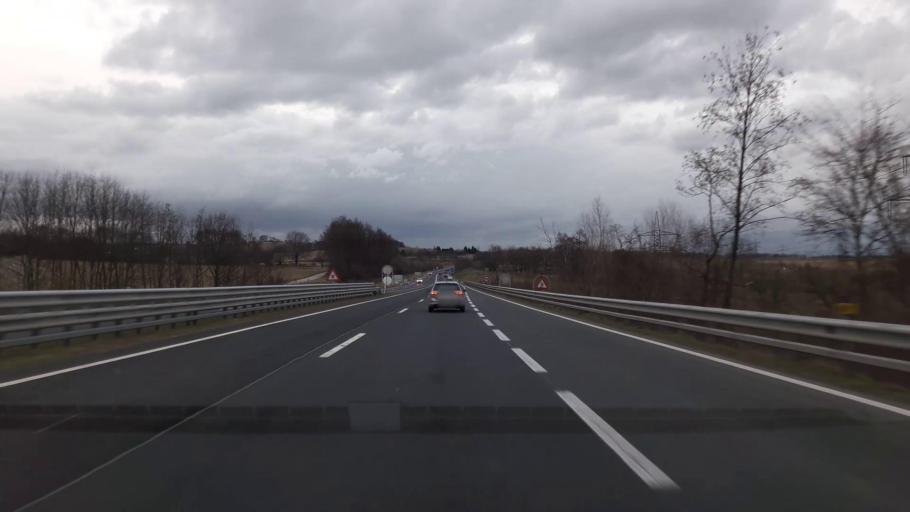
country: AT
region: Burgenland
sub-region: Politischer Bezirk Mattersburg
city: Mattersburg
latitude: 47.7225
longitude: 16.3797
